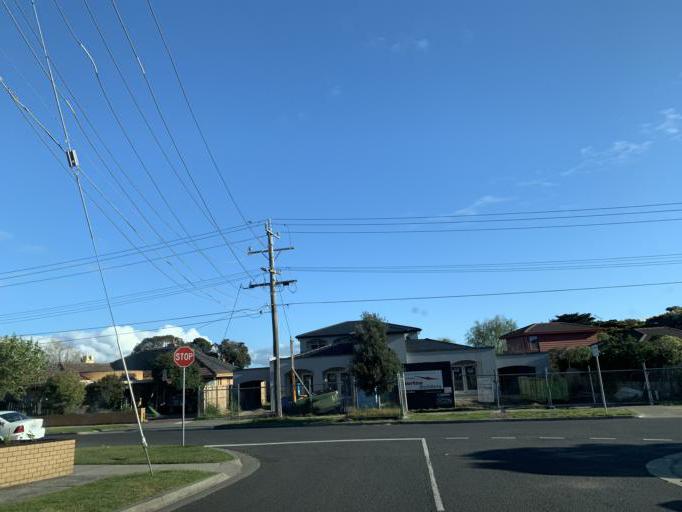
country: AU
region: Victoria
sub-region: Kingston
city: Mentone
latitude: -37.9882
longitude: 145.0656
